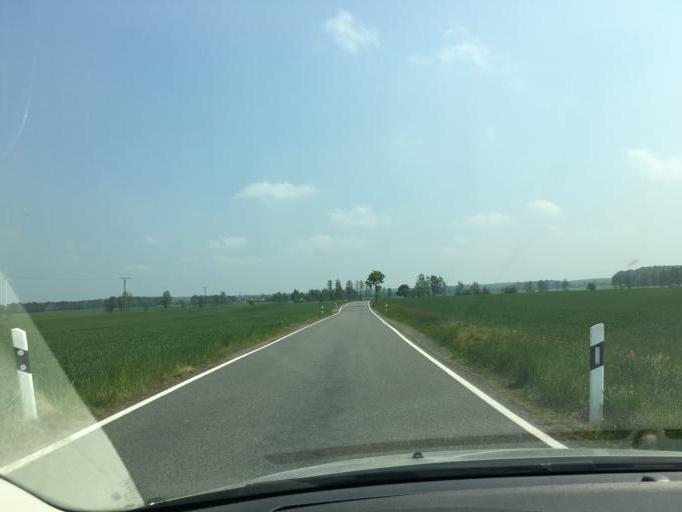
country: DE
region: Saxony
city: Grossbardau
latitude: 51.1836
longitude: 12.6695
